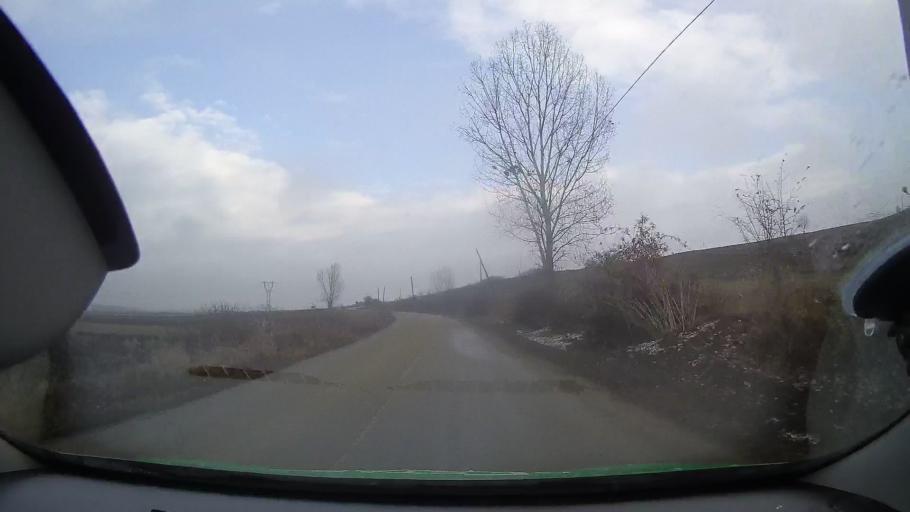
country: RO
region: Alba
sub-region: Comuna Noslac
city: Noslac
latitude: 46.4151
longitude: 23.9687
